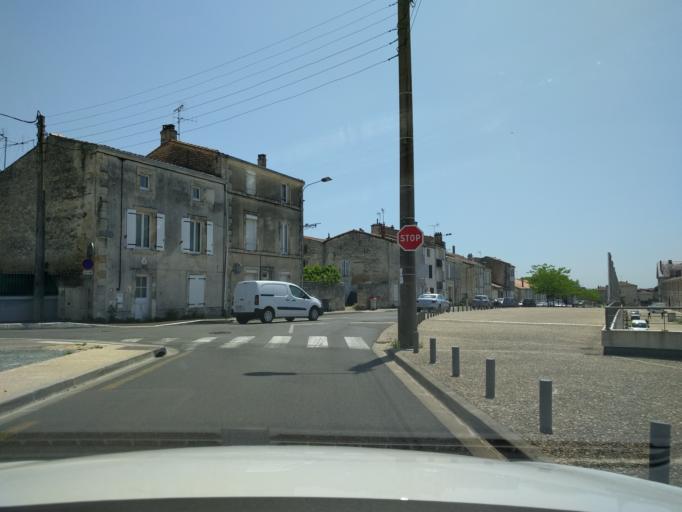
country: FR
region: Poitou-Charentes
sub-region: Departement des Deux-Sevres
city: Niort
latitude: 46.3317
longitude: -0.4598
